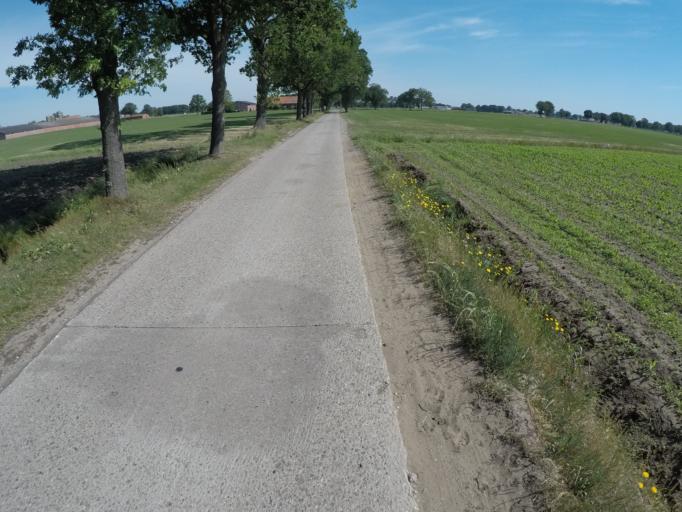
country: BE
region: Flanders
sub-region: Provincie Antwerpen
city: Kalmthout
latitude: 51.3865
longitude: 4.5235
